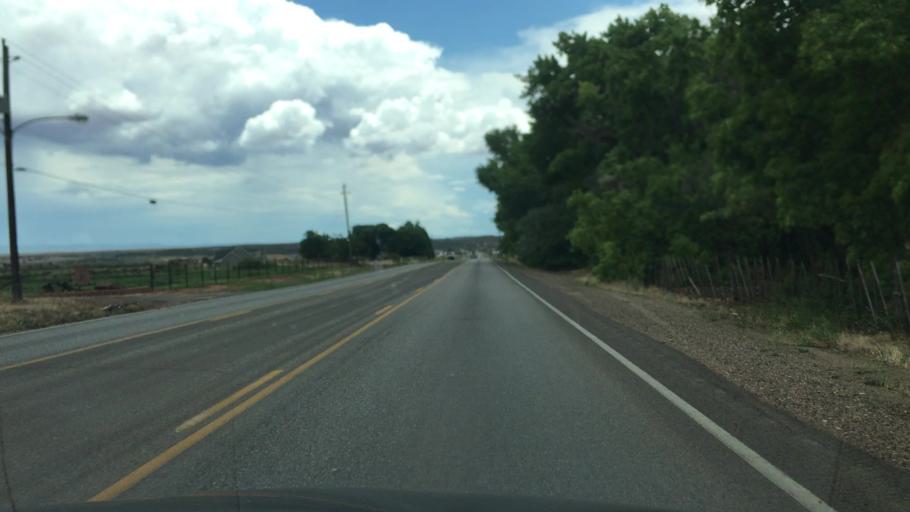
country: US
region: Utah
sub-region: Kane County
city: Kanab
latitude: 37.0287
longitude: -112.5249
